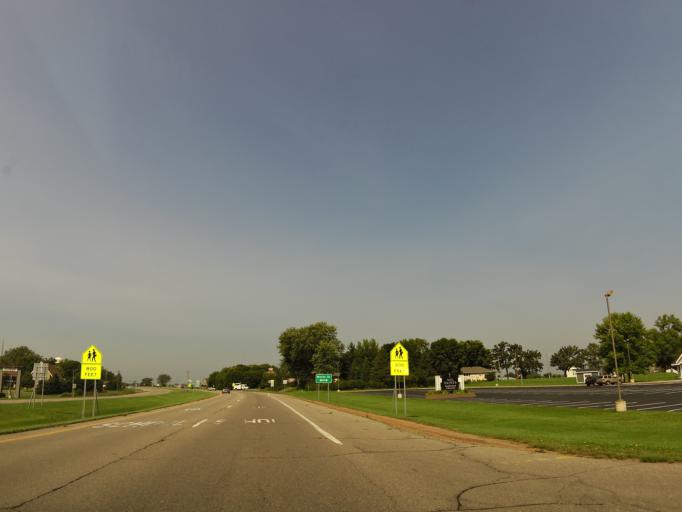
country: US
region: Minnesota
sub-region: Carver County
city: Norwood Young America
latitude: 44.7720
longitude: -93.9218
